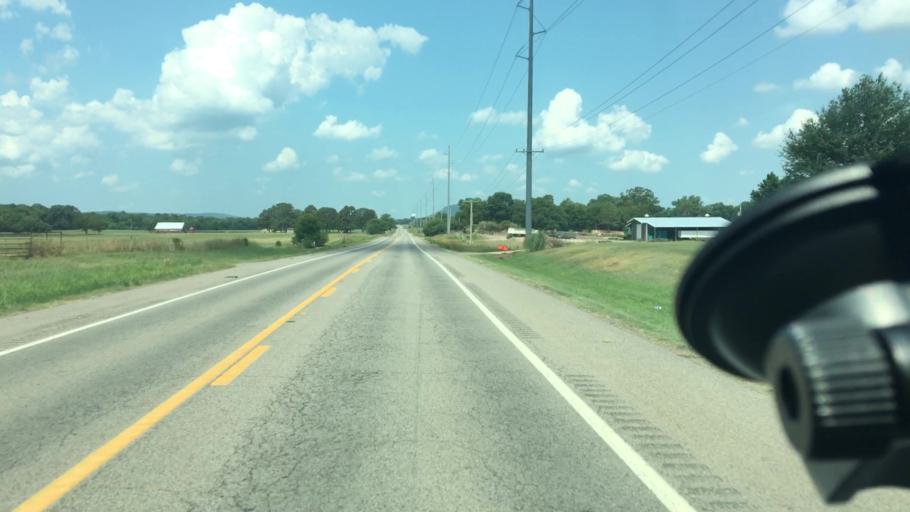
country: US
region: Arkansas
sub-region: Logan County
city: Paris
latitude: 35.2947
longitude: -93.6614
